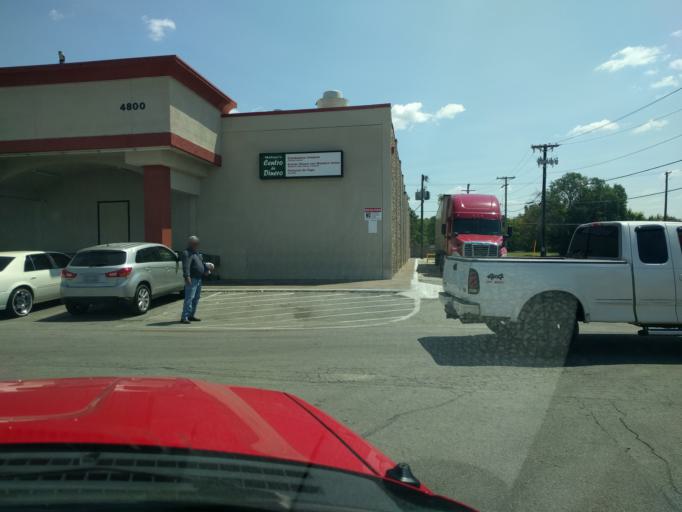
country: US
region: Texas
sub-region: Dallas County
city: Dallas
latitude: 32.7940
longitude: -96.7640
